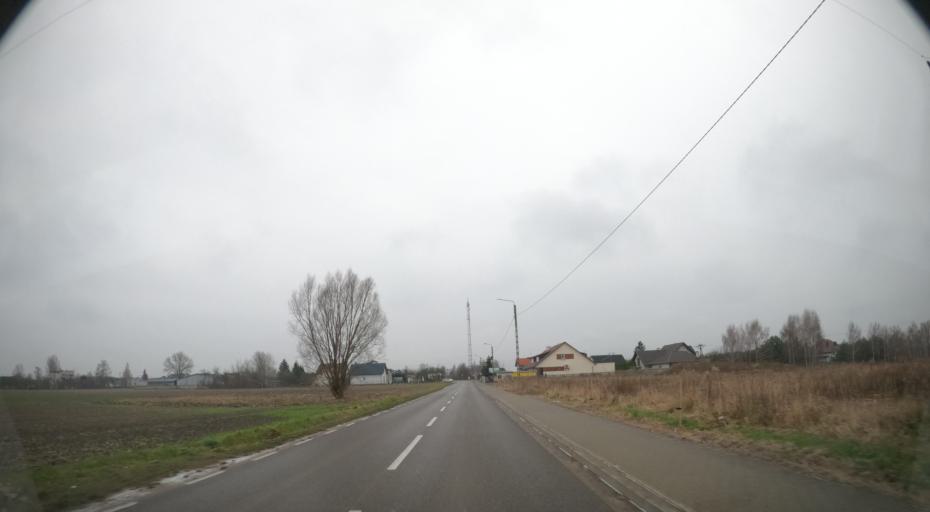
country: PL
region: Masovian Voivodeship
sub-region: Powiat radomski
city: Skaryszew
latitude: 51.3794
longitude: 21.2530
